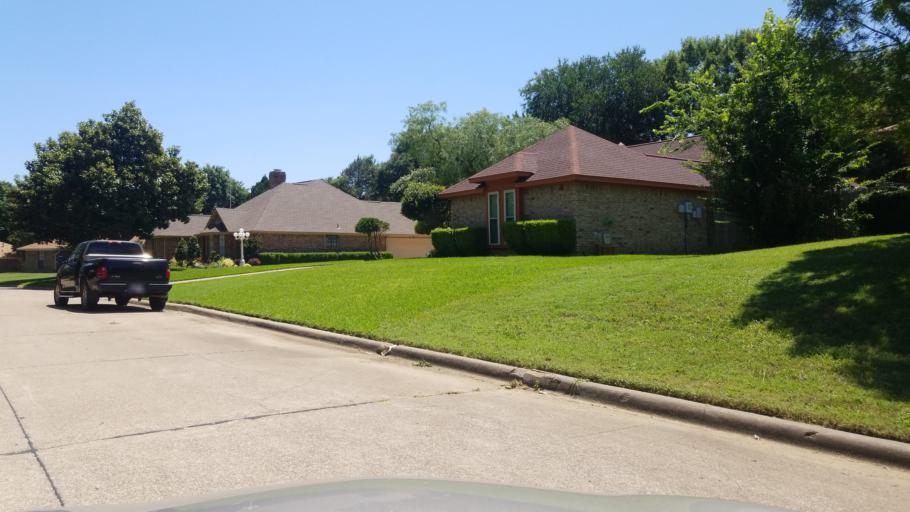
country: US
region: Texas
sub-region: Dallas County
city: Grand Prairie
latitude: 32.6815
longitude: -97.0011
